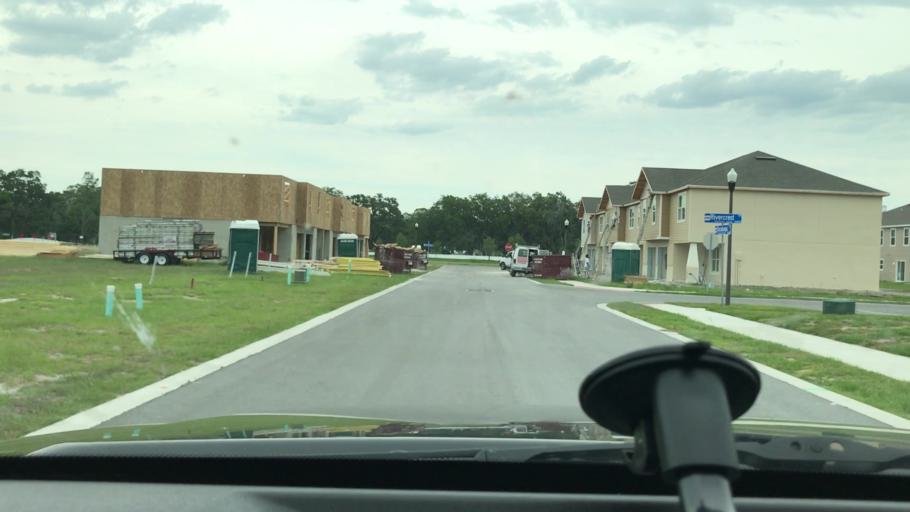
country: US
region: Florida
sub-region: Hillsborough County
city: Riverview
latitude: 27.8592
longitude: -82.3309
